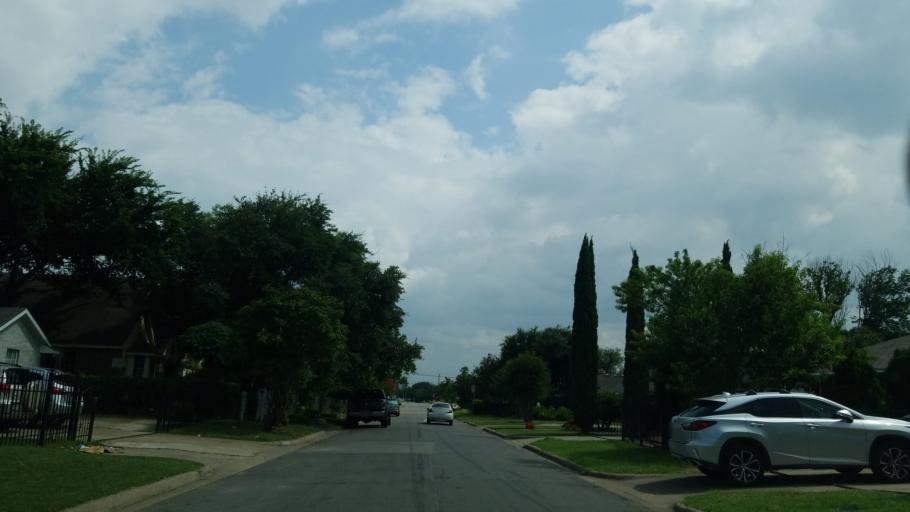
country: US
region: Texas
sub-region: Dallas County
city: University Park
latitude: 32.8392
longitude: -96.8312
